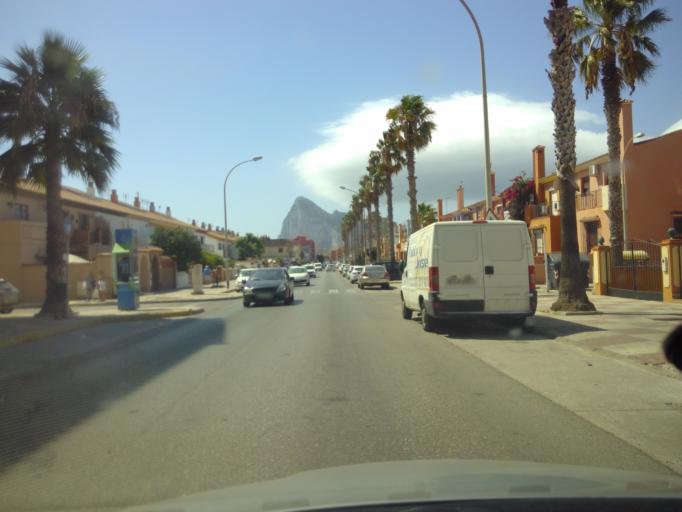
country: ES
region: Andalusia
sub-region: Provincia de Cadiz
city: La Linea de la Concepcion
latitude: 36.1760
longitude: -5.3488
